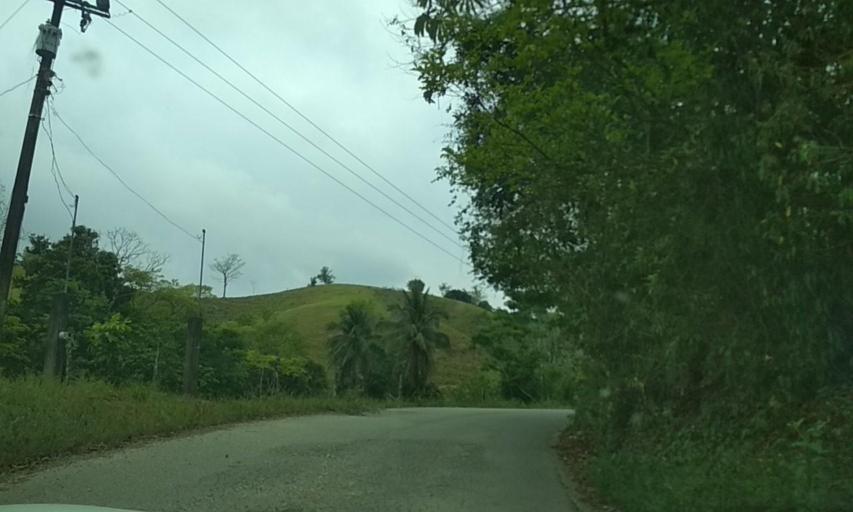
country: MX
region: Veracruz
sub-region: Uxpanapa
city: Poblado 10
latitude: 17.4955
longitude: -94.1391
